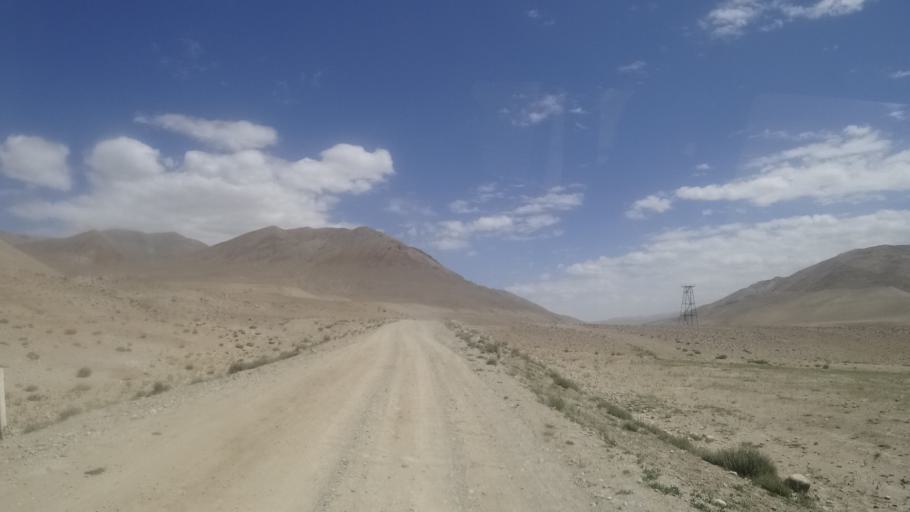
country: AF
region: Badakhshan
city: Khandud
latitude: 37.2950
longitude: 72.9650
